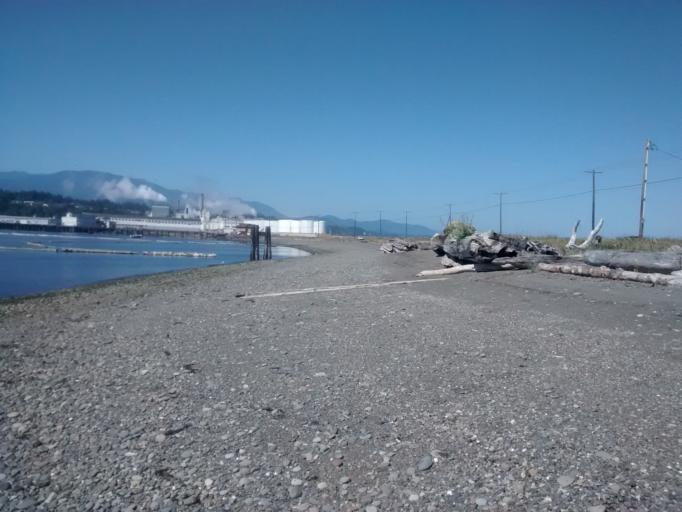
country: US
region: Washington
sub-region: Clallam County
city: Port Angeles
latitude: 48.1387
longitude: -123.4557
